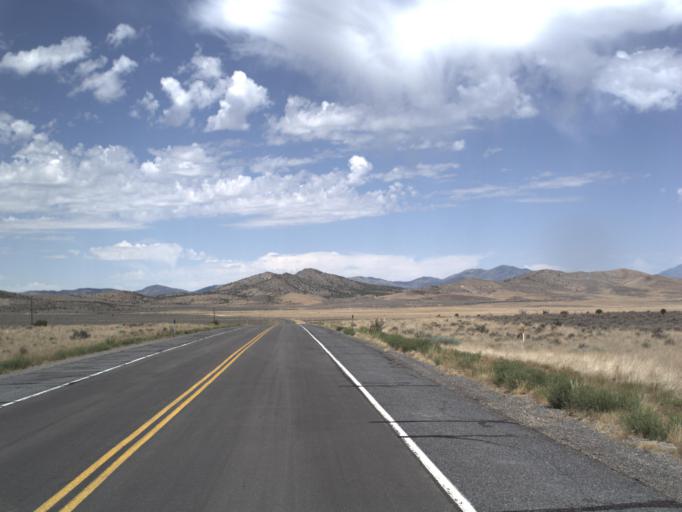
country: US
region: Utah
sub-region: Utah County
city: Eagle Mountain
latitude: 40.0678
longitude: -112.3263
